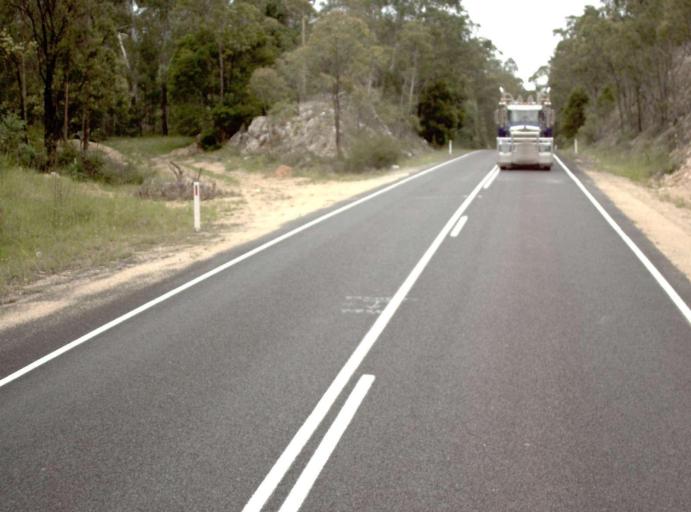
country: AU
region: New South Wales
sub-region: Bombala
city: Bombala
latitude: -37.3257
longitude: 149.2068
